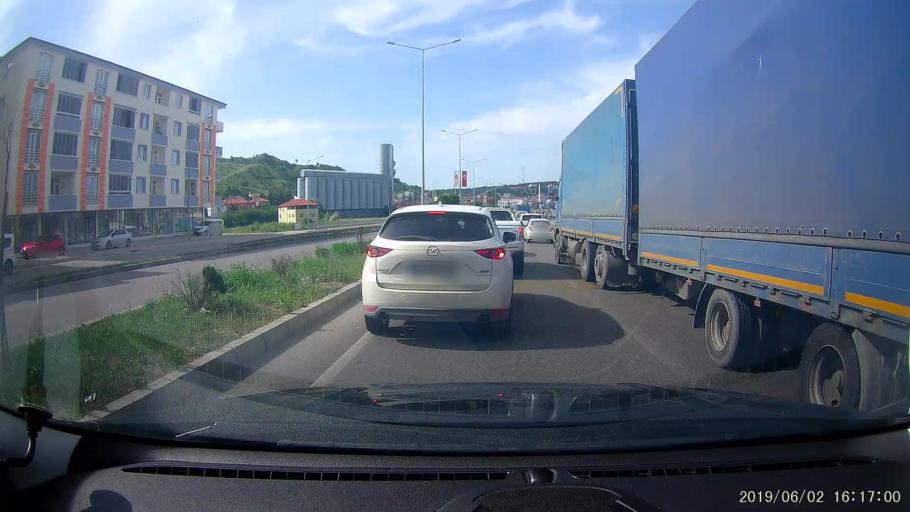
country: TR
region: Samsun
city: Havza
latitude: 40.9590
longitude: 35.6660
